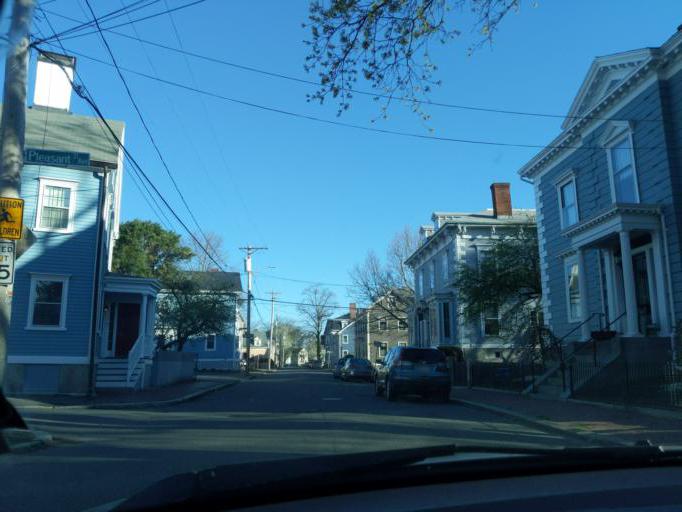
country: US
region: Massachusetts
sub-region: Essex County
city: Salem
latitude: 42.5258
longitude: -70.8889
